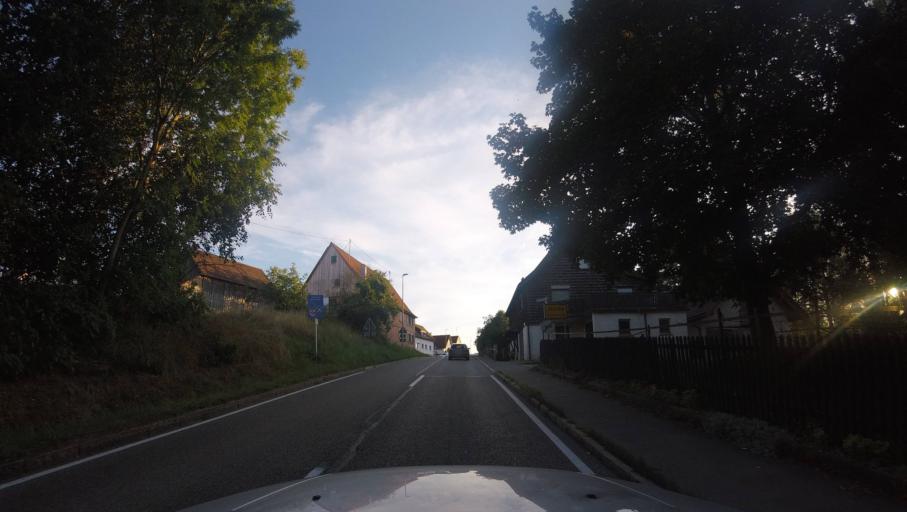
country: DE
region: Baden-Wuerttemberg
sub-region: Regierungsbezirk Stuttgart
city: Althutte
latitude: 48.9212
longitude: 9.5777
